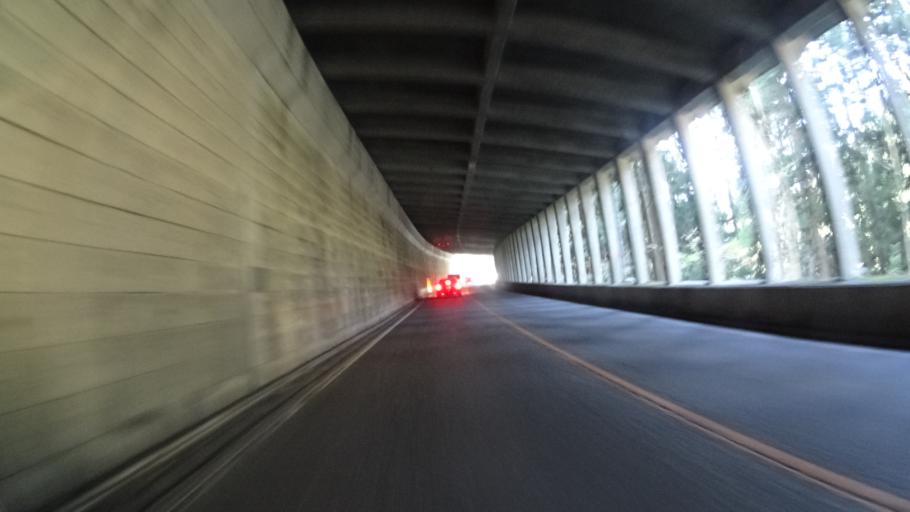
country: JP
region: Ishikawa
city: Tsurugi-asahimachi
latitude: 36.3731
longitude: 136.5819
